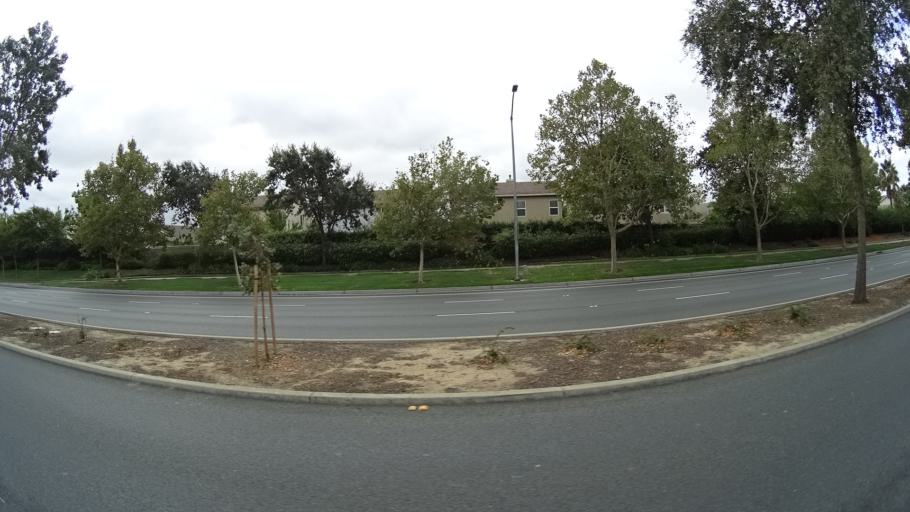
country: US
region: California
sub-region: Sacramento County
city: Laguna
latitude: 38.4089
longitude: -121.4323
